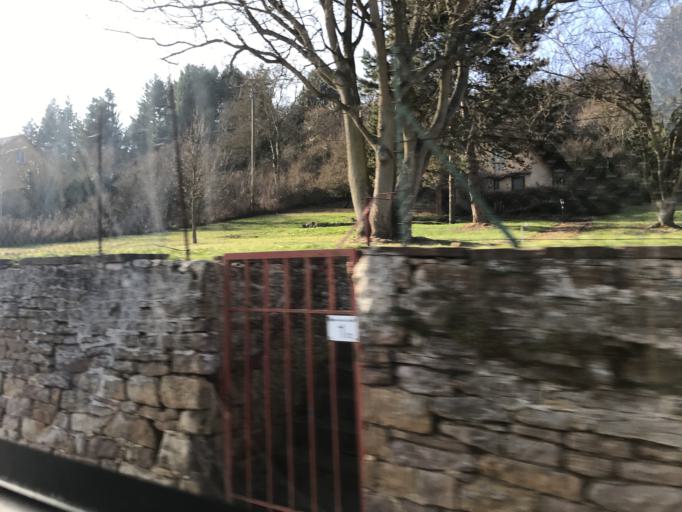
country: DE
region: Rheinland-Pfalz
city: Obermoschel
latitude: 49.7284
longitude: 7.7708
